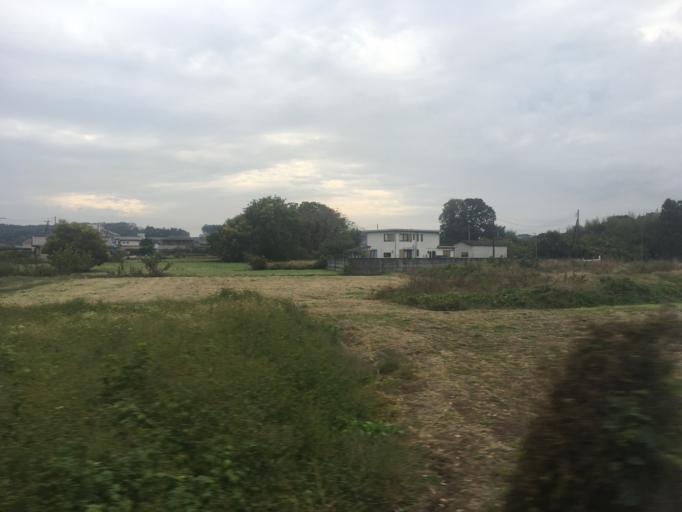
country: JP
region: Saitama
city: Morohongo
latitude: 35.9016
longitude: 139.3534
